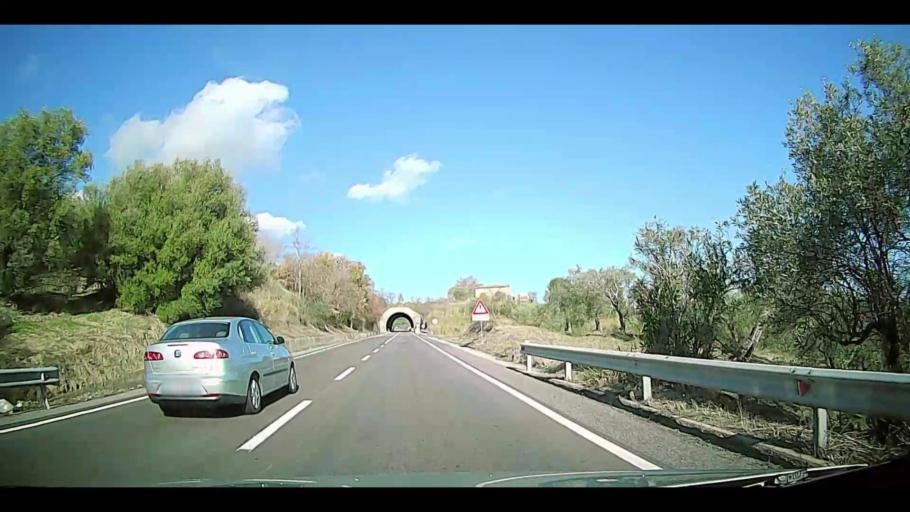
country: IT
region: Calabria
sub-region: Provincia di Crotone
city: Caccuri
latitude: 39.2176
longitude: 16.7961
